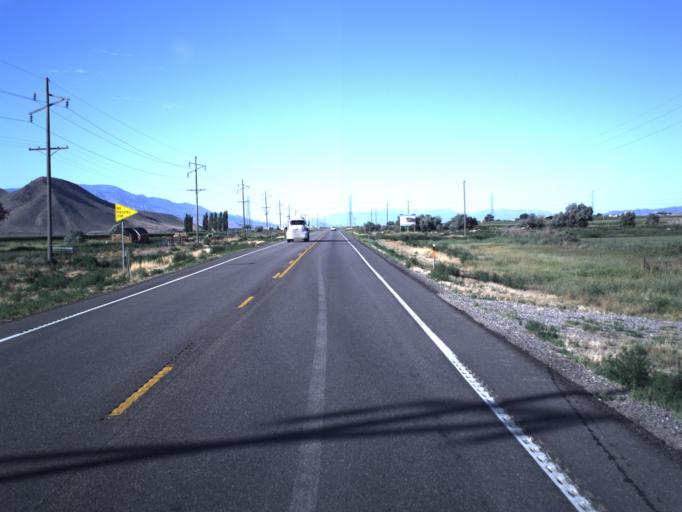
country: US
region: Utah
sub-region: Sevier County
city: Aurora
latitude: 38.9088
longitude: -111.9365
